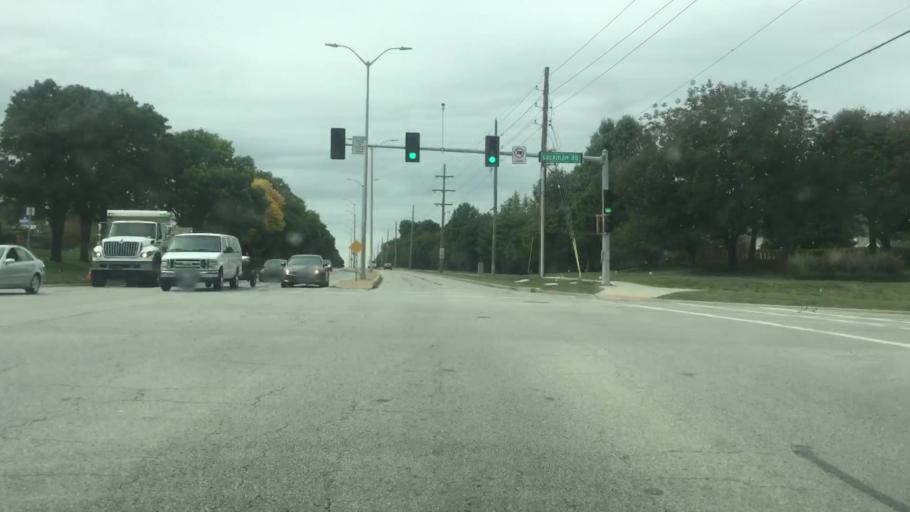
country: US
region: Kansas
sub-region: Johnson County
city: Lenexa
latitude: 38.9565
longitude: -94.7608
